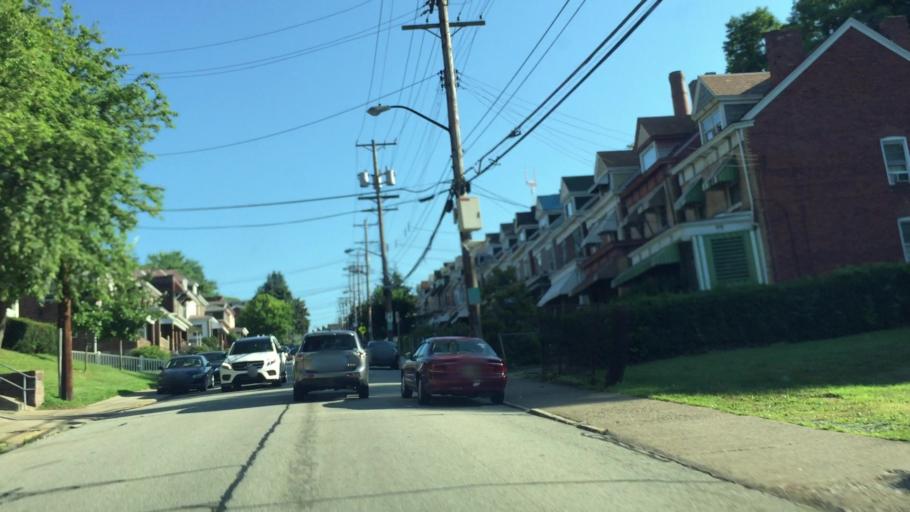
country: US
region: Pennsylvania
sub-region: Allegheny County
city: Bloomfield
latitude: 40.4388
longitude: -79.9654
